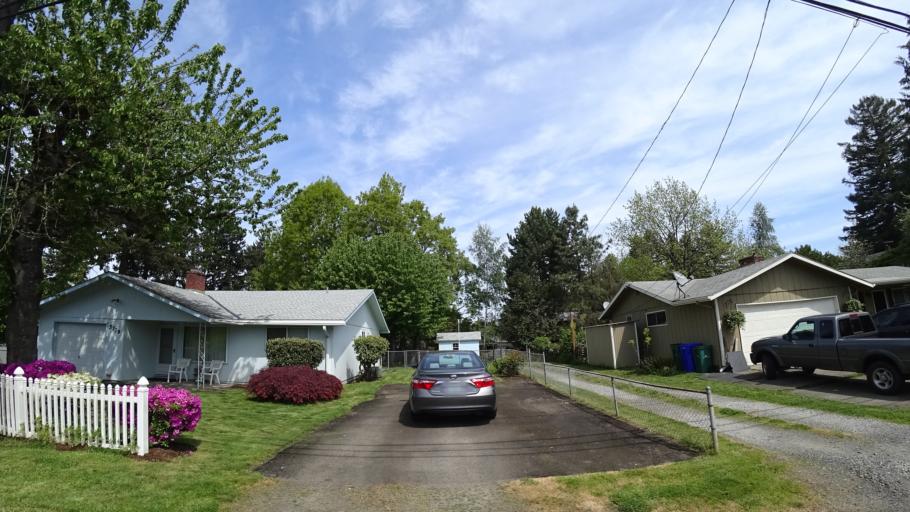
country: US
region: Oregon
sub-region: Clackamas County
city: Oatfield
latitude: 45.4446
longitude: -122.6033
